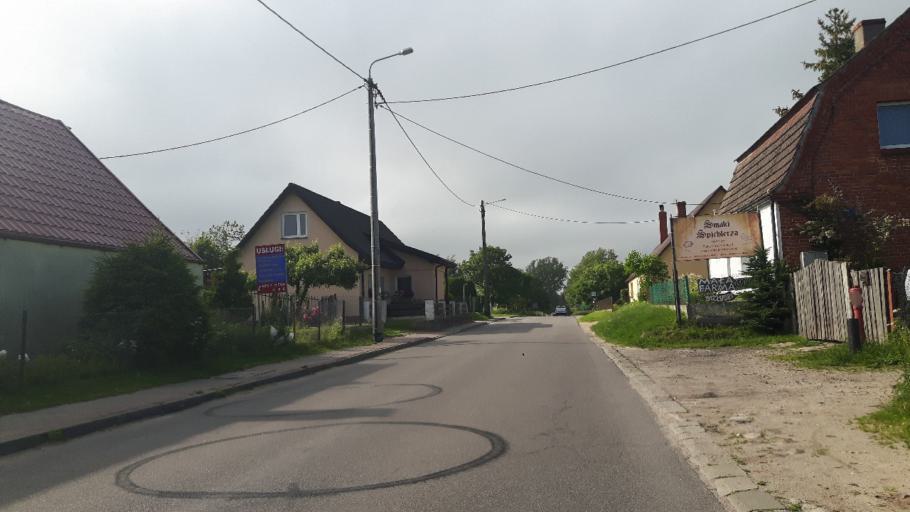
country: PL
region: Pomeranian Voivodeship
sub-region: Slupsk
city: Slupsk
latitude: 54.6169
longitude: 17.0309
